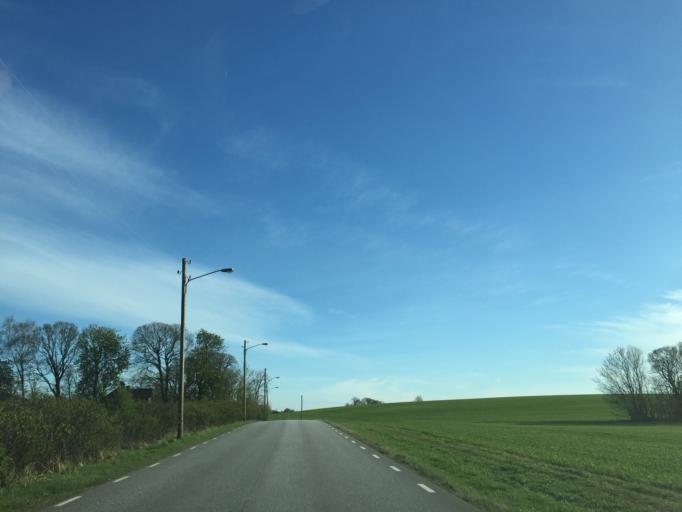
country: SE
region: Skane
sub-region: Malmo
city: Oxie
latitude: 55.5786
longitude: 13.0965
